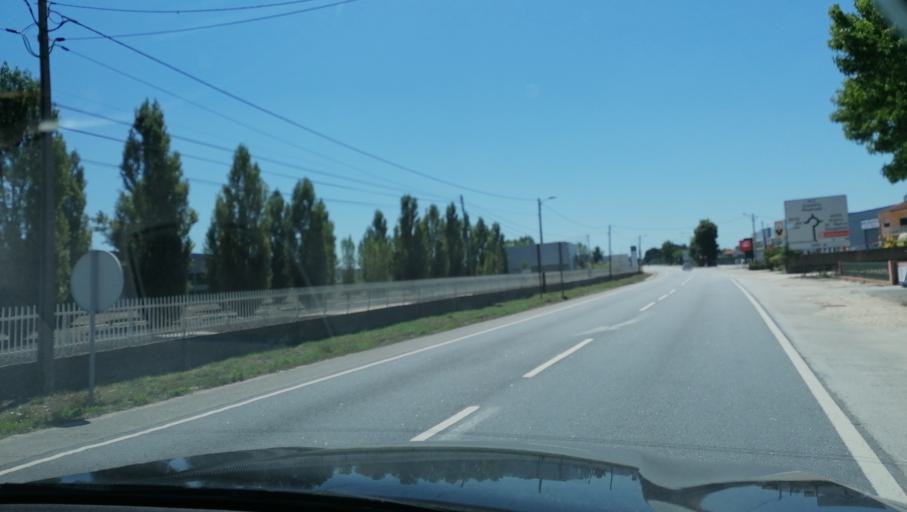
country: PT
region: Aveiro
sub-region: Anadia
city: Arcos
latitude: 40.4640
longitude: -8.4563
